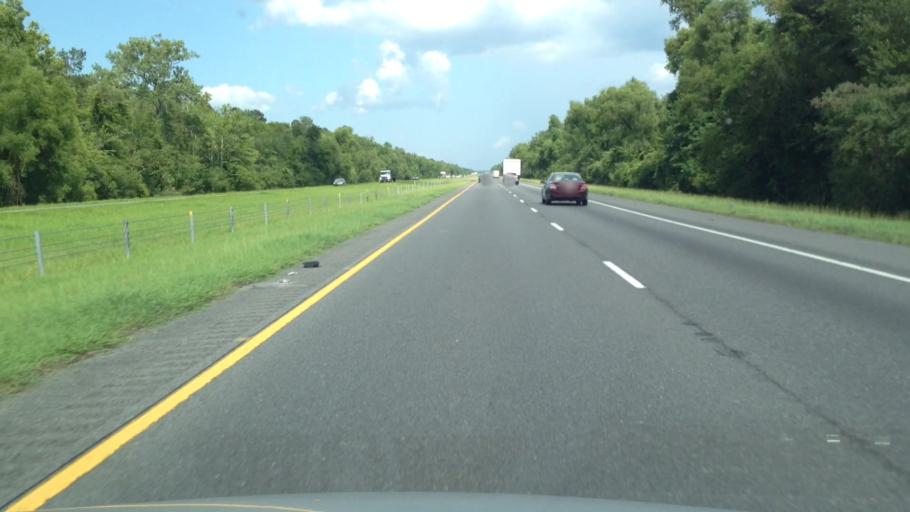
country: US
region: Louisiana
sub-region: Saint James Parish
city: Grand Point
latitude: 30.1374
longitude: -90.7391
